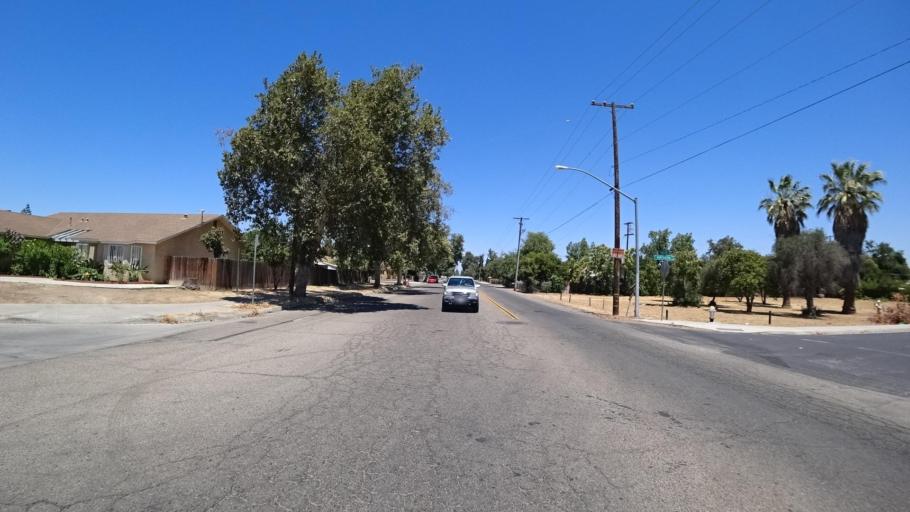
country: US
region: California
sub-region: Fresno County
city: Sunnyside
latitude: 36.7395
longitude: -119.7274
